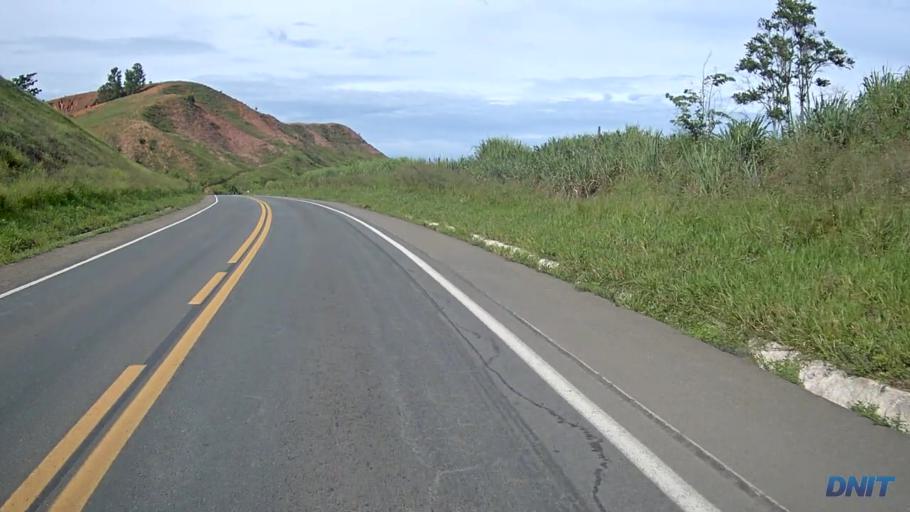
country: BR
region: Minas Gerais
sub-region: Belo Oriente
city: Belo Oriente
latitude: -19.1767
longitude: -42.2559
